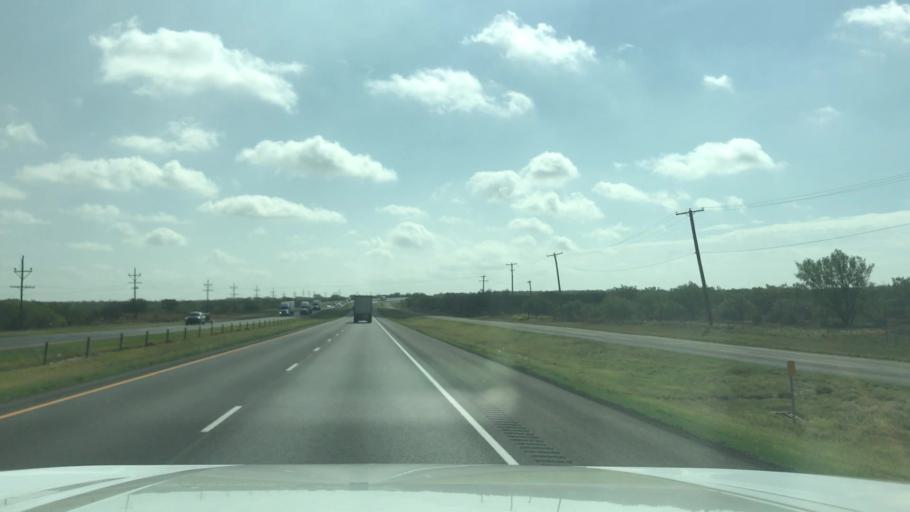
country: US
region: Texas
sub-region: Nolan County
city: Sweetwater
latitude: 32.4956
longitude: -100.2774
